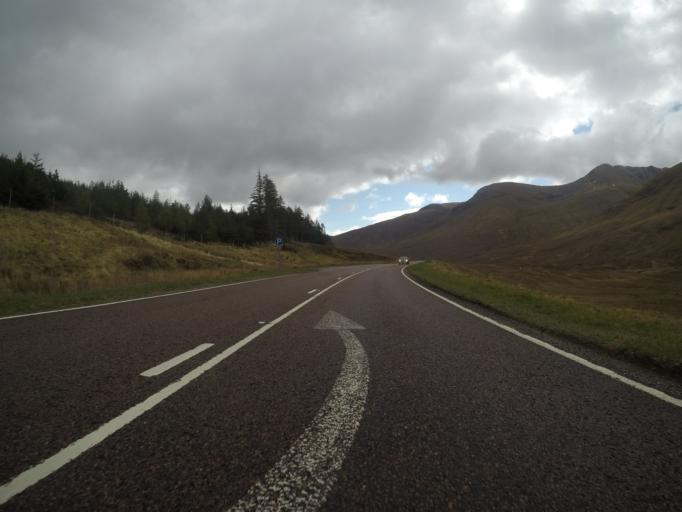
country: GB
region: Scotland
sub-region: Highland
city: Fort William
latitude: 57.1526
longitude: -5.2363
